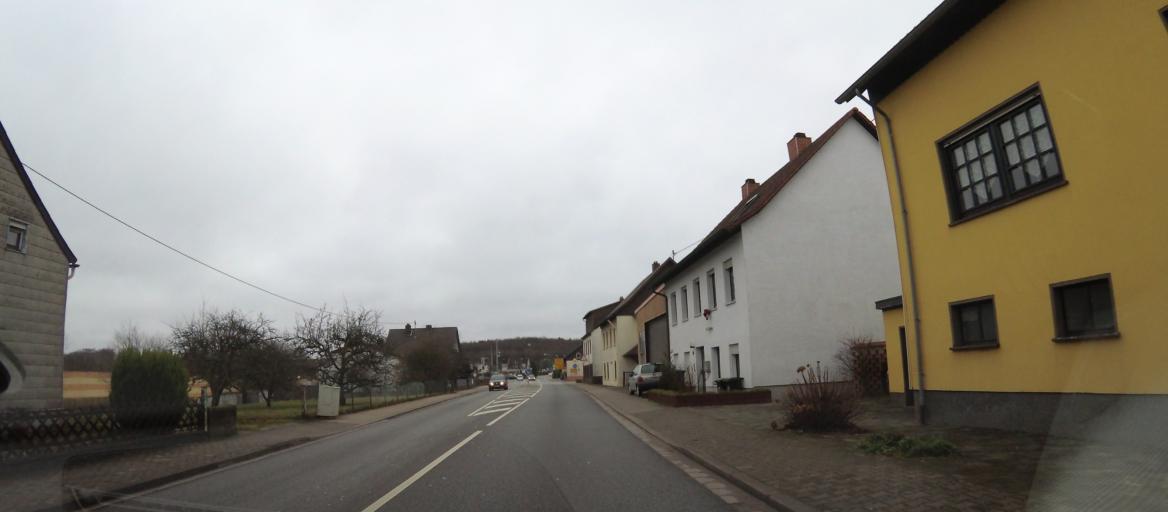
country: DE
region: Saarland
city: Merchweiler
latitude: 49.3622
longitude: 7.0670
